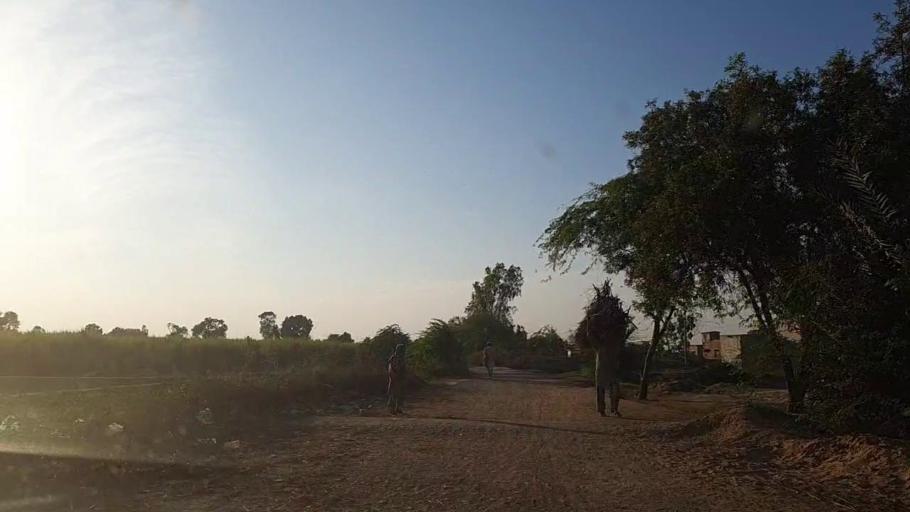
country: PK
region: Sindh
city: Mirpur Batoro
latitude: 24.6816
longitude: 68.2146
